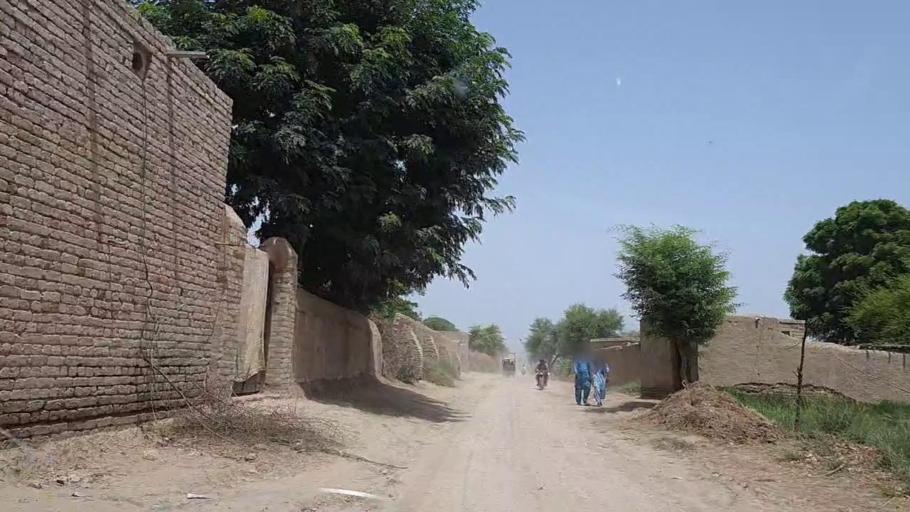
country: PK
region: Sindh
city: Tharu Shah
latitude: 26.9046
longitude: 68.0061
